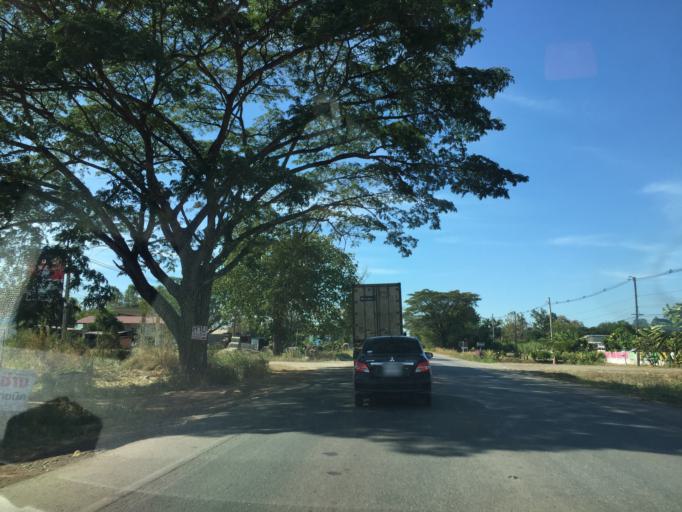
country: TH
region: Changwat Nong Bua Lamphu
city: Na Klang
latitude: 17.3205
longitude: 102.1471
